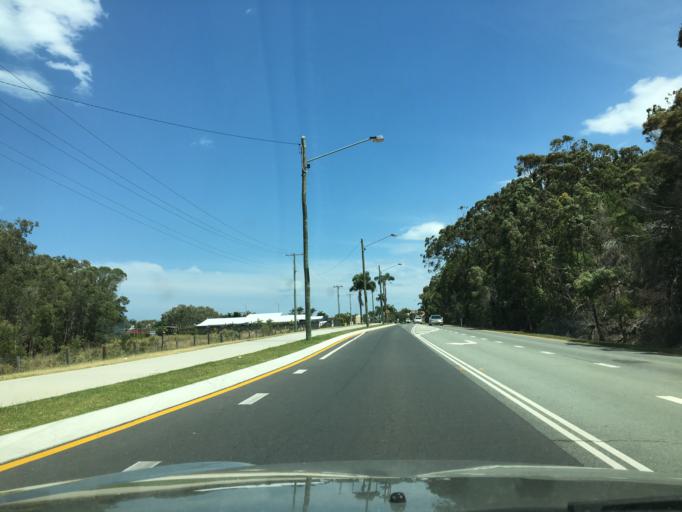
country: AU
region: Queensland
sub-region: Moreton Bay
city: Bongaree
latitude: -27.0771
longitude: 153.1370
